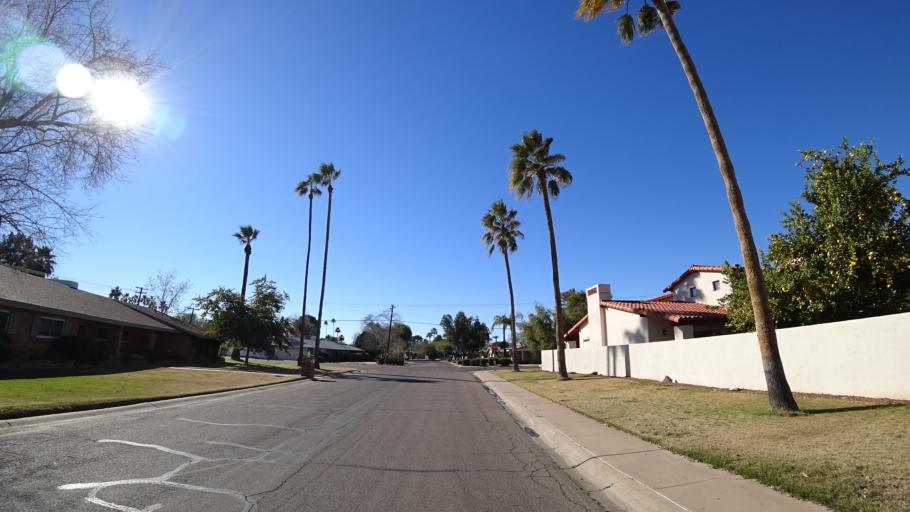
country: US
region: Arizona
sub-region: Maricopa County
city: Phoenix
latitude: 33.5451
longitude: -112.0777
